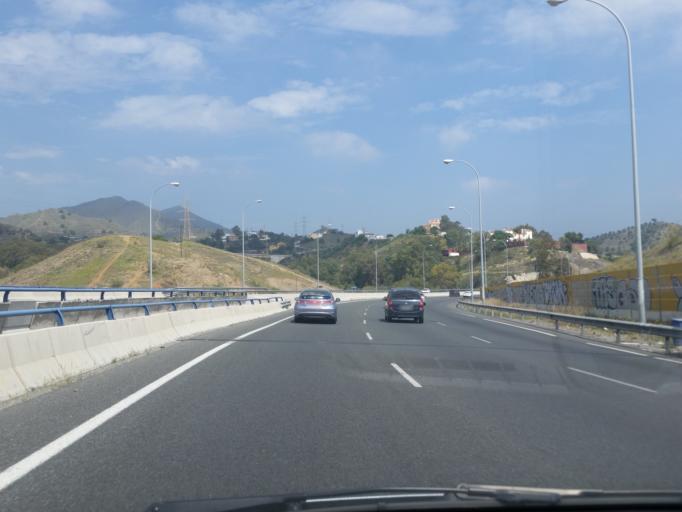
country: ES
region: Andalusia
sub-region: Provincia de Malaga
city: Malaga
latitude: 36.7370
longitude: -4.4542
